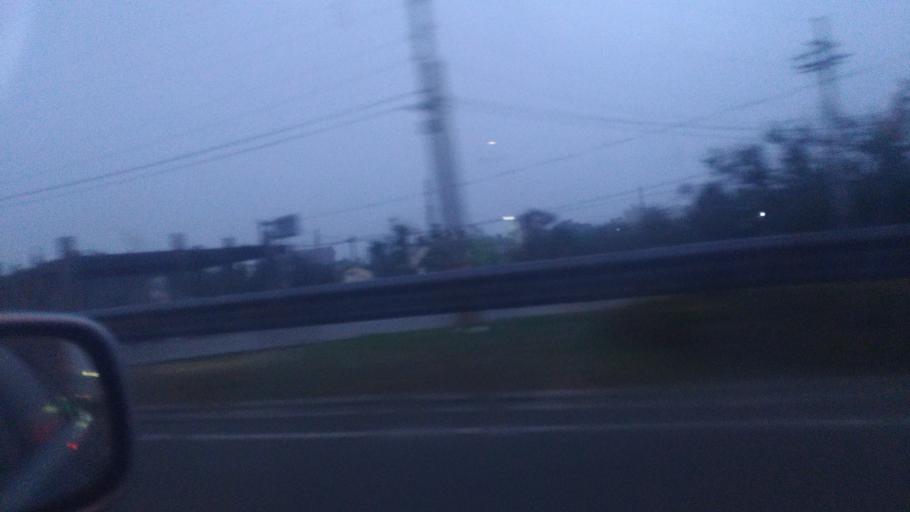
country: TW
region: Taiwan
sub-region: Miaoli
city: Miaoli
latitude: 24.4609
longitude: 120.6521
